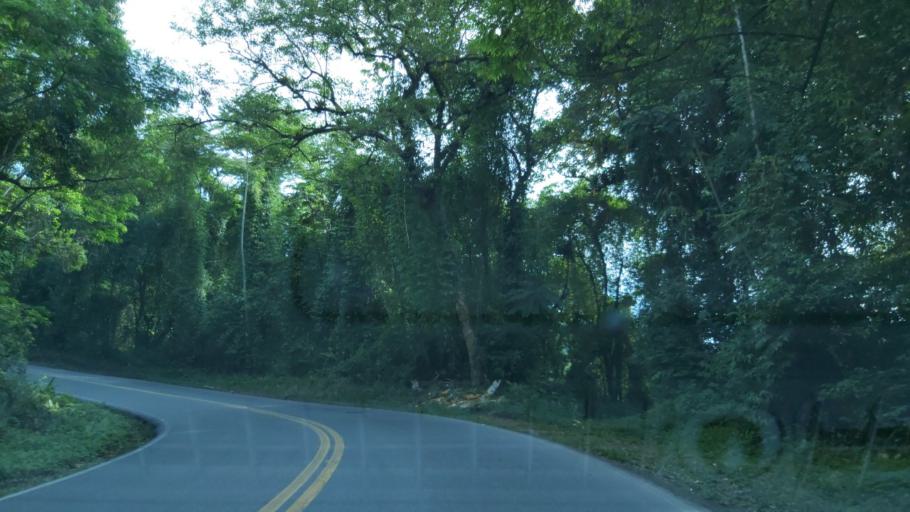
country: BR
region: Sao Paulo
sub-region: Juquia
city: Juquia
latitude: -24.1016
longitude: -47.6259
